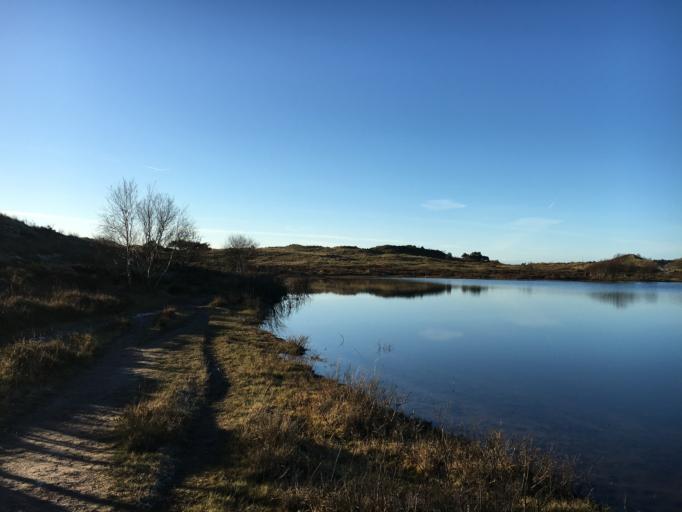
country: NL
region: North Holland
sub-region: Gemeente Bergen
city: Egmond aan Zee
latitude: 52.7031
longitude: 4.6657
